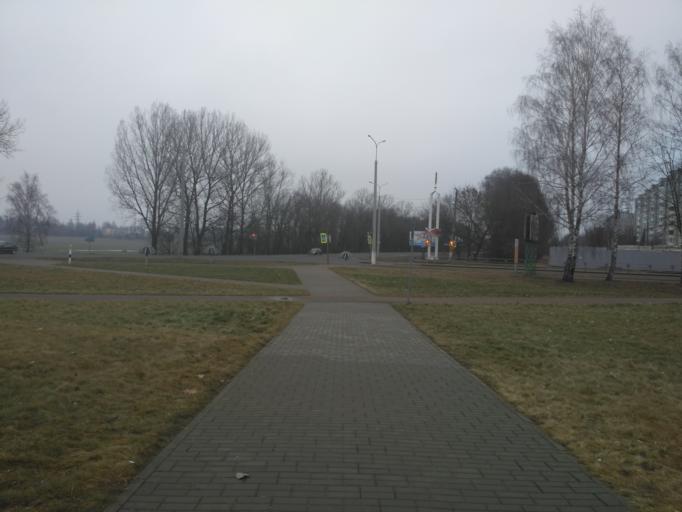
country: BY
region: Brest
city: Baranovichi
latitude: 53.1546
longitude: 25.9955
